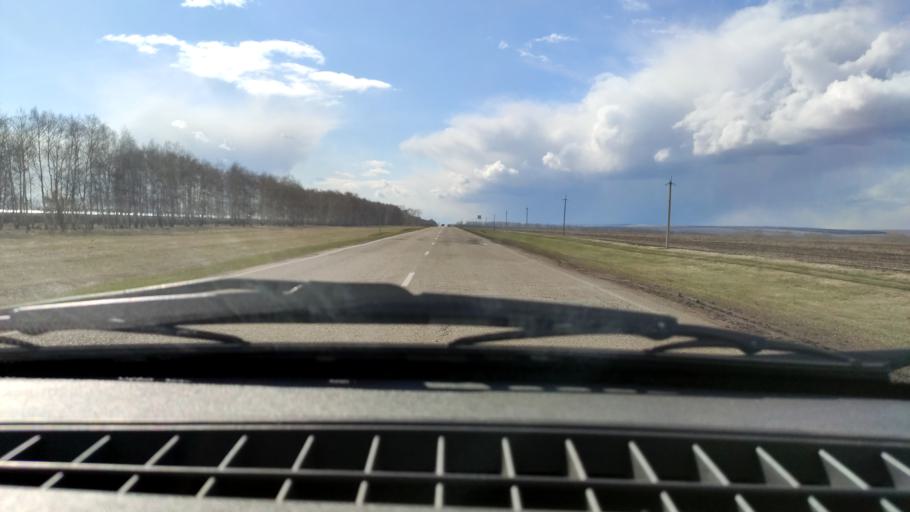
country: RU
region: Bashkortostan
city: Kushnarenkovo
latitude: 55.1040
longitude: 55.0276
